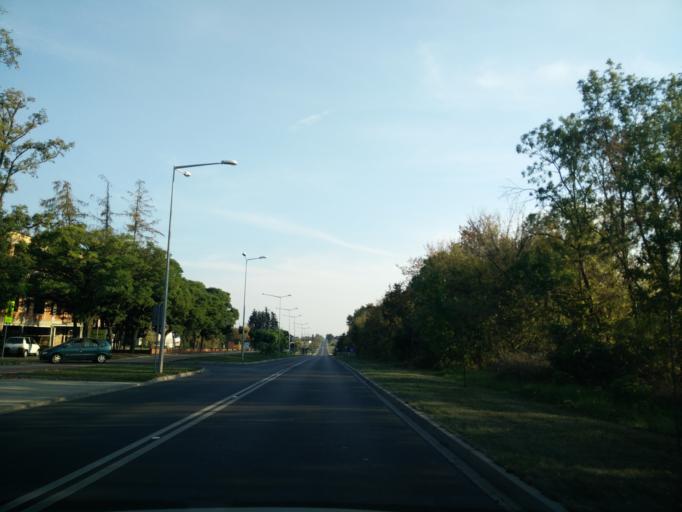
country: PL
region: Greater Poland Voivodeship
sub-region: Powiat sredzki
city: Sroda Wielkopolska
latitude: 52.2172
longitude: 17.2915
